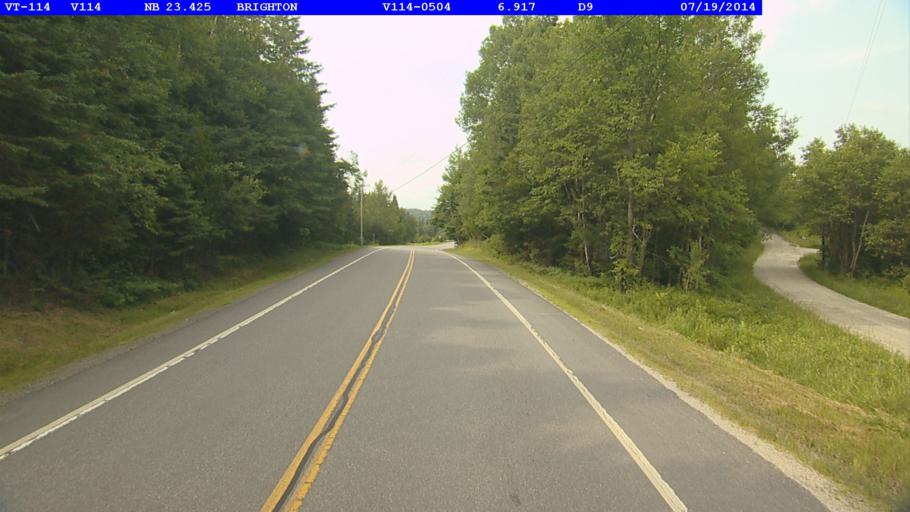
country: CA
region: Quebec
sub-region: Estrie
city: Coaticook
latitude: 44.8405
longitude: -71.9069
